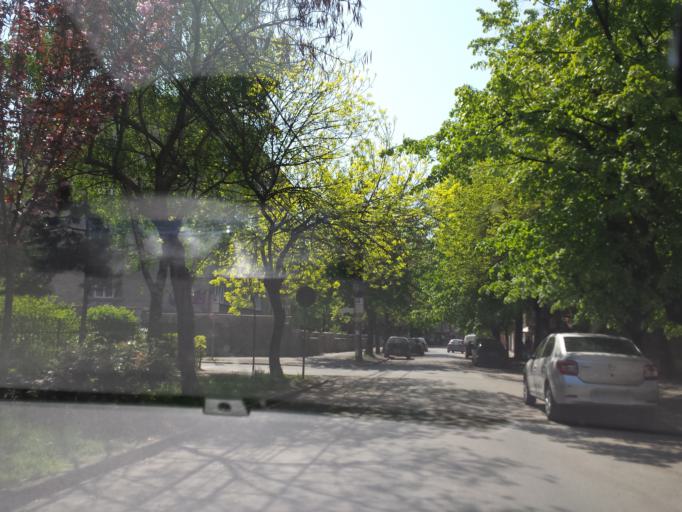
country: RO
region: Timis
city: Timisoara
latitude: 45.7565
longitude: 21.2353
